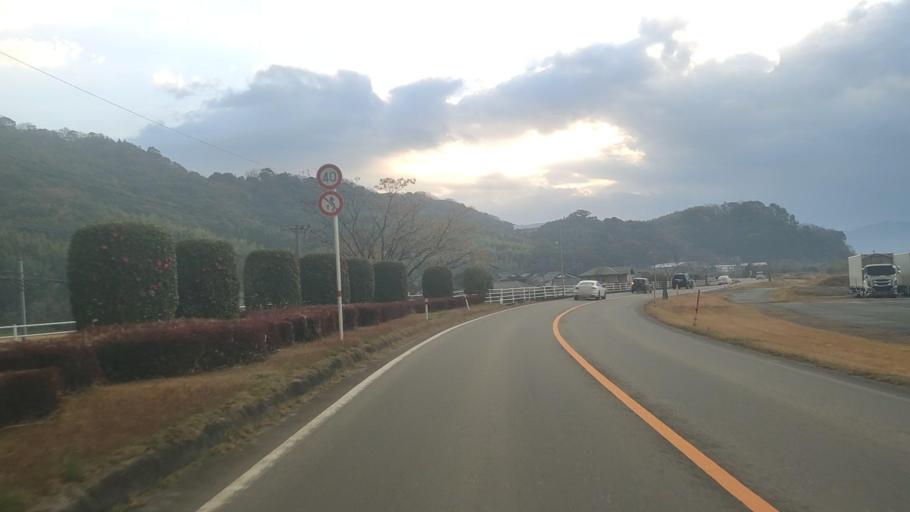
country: JP
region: Kumamoto
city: Uto
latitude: 32.7010
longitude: 130.7820
